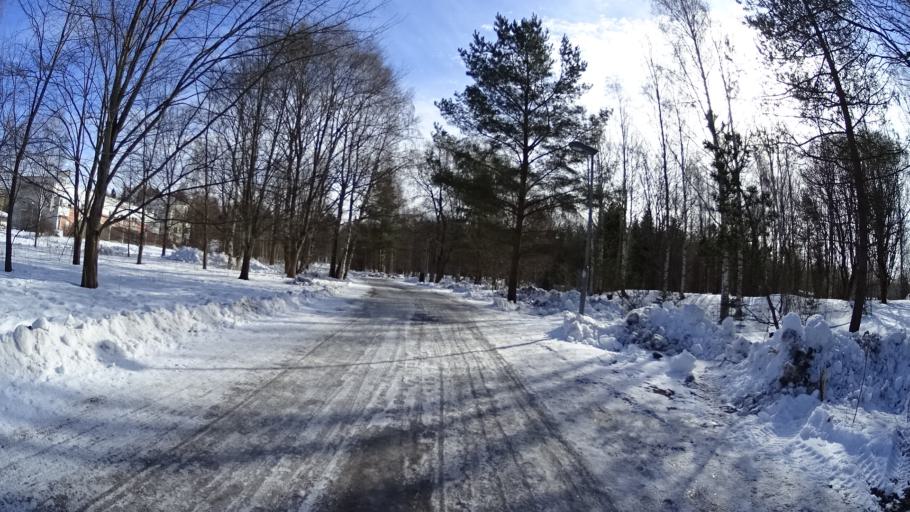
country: FI
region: Uusimaa
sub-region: Helsinki
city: Teekkarikylae
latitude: 60.2061
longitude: 24.8586
